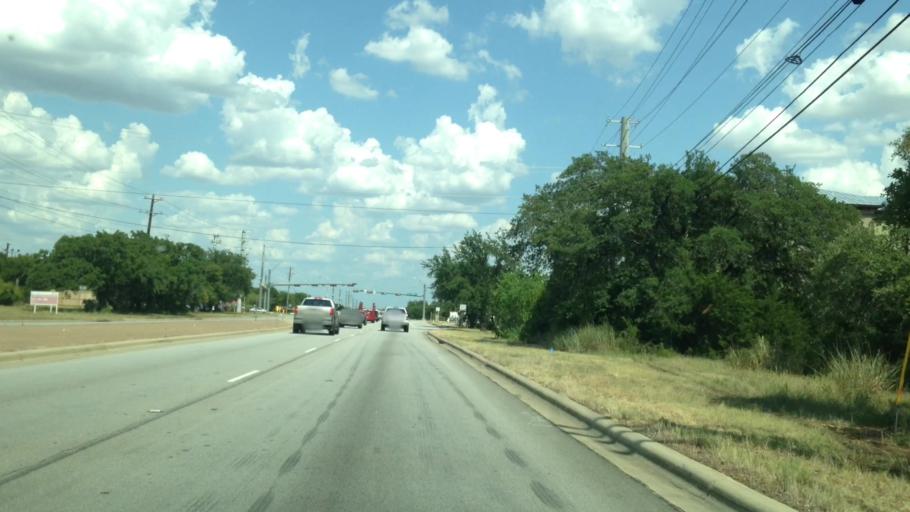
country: US
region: Texas
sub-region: Williamson County
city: Georgetown
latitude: 30.6328
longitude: -97.7027
